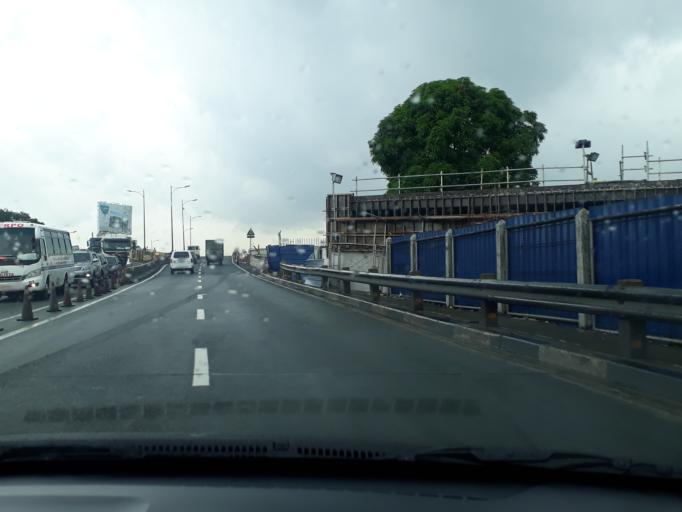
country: PH
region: Metro Manila
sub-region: Makati City
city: Makati City
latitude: 14.5130
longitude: 121.0335
